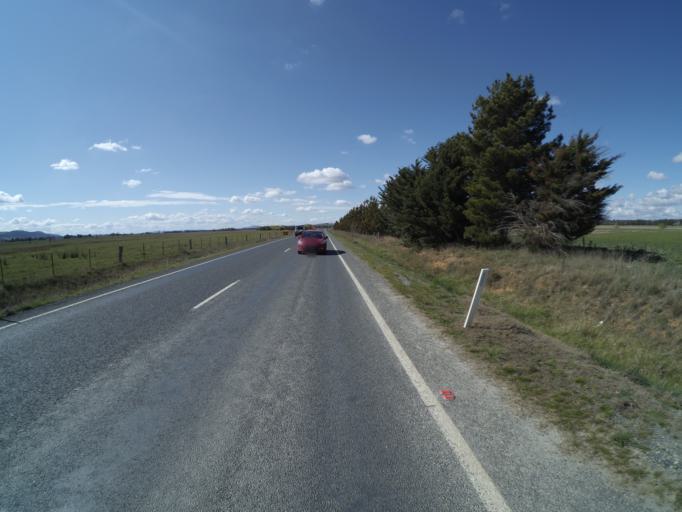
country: AU
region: New South Wales
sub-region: Palerang
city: Bungendore
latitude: -35.2754
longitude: 149.4254
